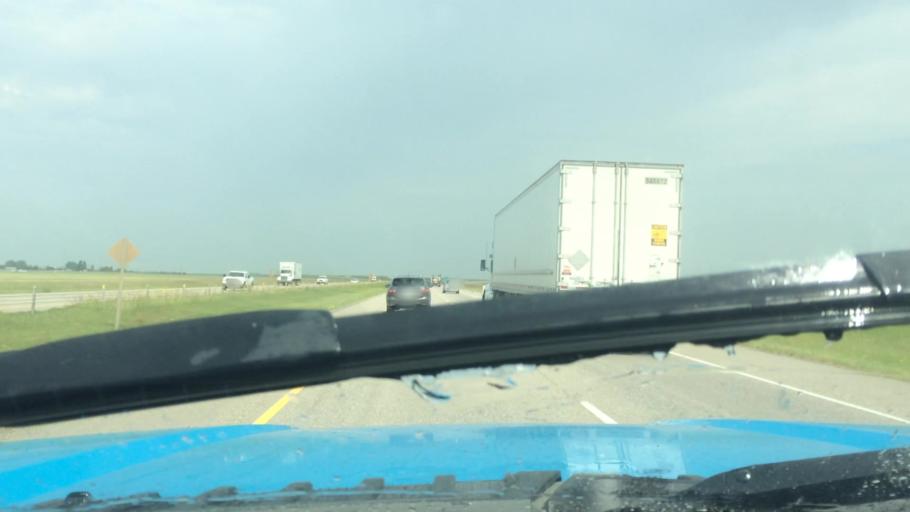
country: CA
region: Alberta
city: Didsbury
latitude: 51.6528
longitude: -114.0254
